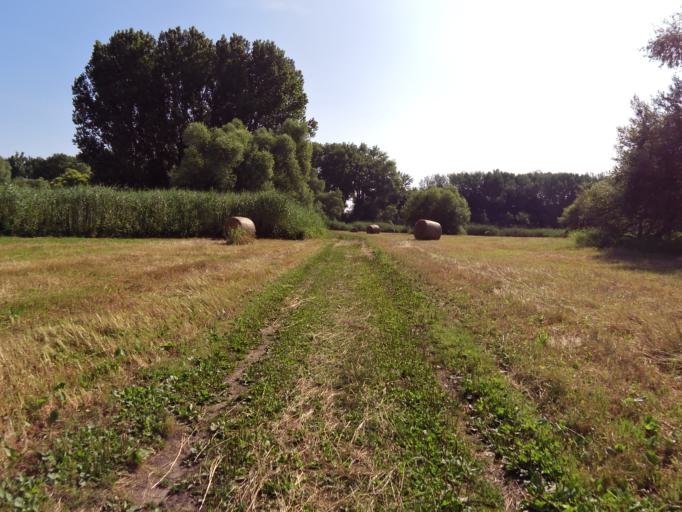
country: DE
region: Hesse
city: Lampertheim
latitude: 49.6035
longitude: 8.4287
